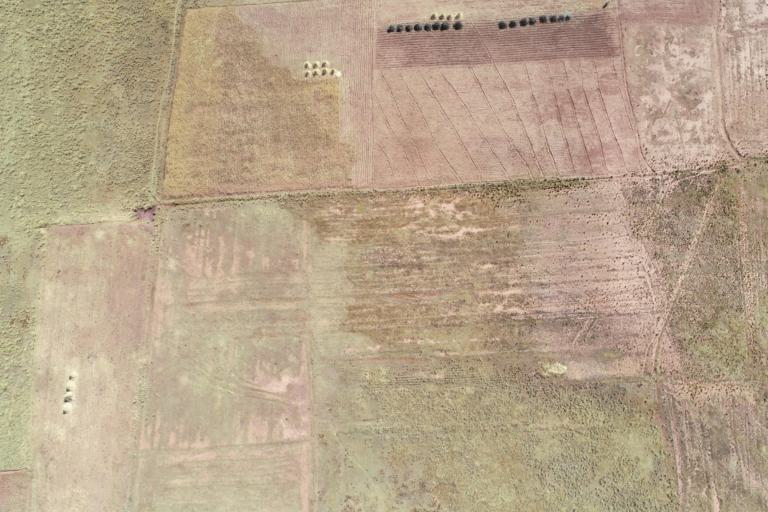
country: BO
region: La Paz
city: Tiahuanaco
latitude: -16.5919
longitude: -68.7555
